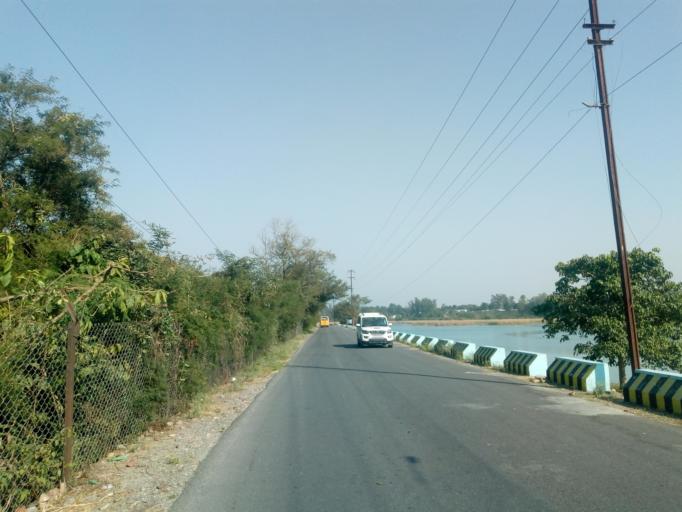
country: IN
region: Himachal Pradesh
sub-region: Sirmaur
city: Paonta Sahib
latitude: 30.4399
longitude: 77.6698
